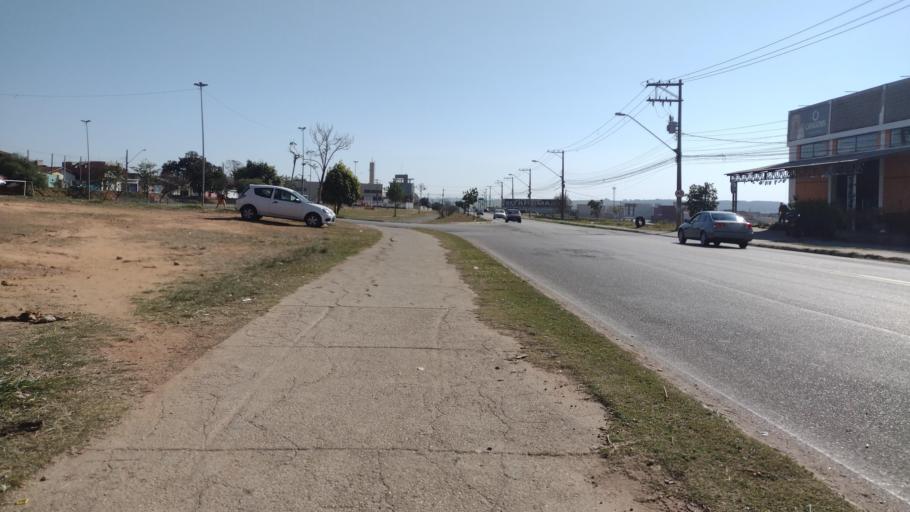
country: BR
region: Sao Paulo
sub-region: Sorocaba
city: Sorocaba
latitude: -23.4260
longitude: -47.4830
